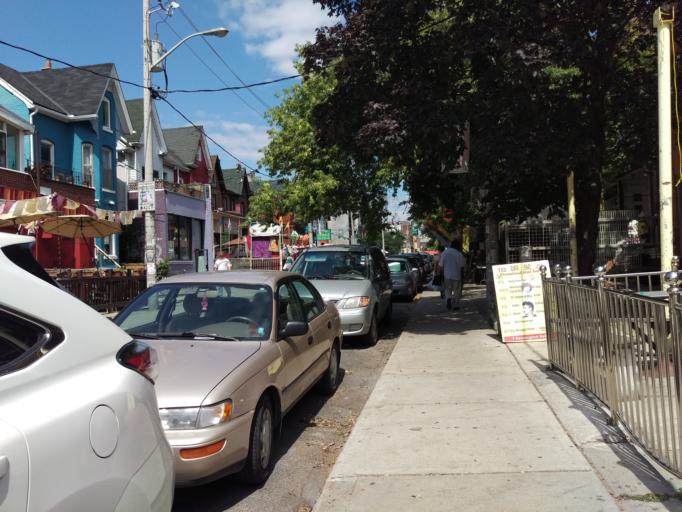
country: CA
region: Ontario
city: Toronto
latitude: 43.6527
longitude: -79.3999
